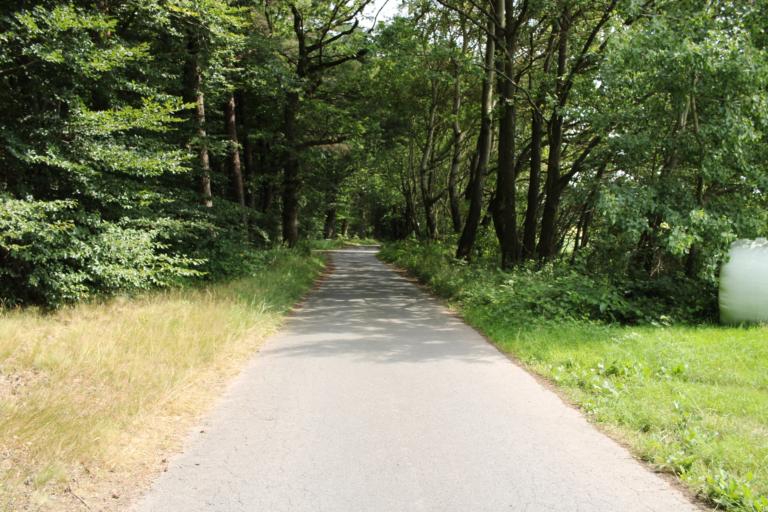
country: DE
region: Hesse
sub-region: Regierungsbezirk Darmstadt
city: Erbach
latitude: 49.6620
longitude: 8.9420
